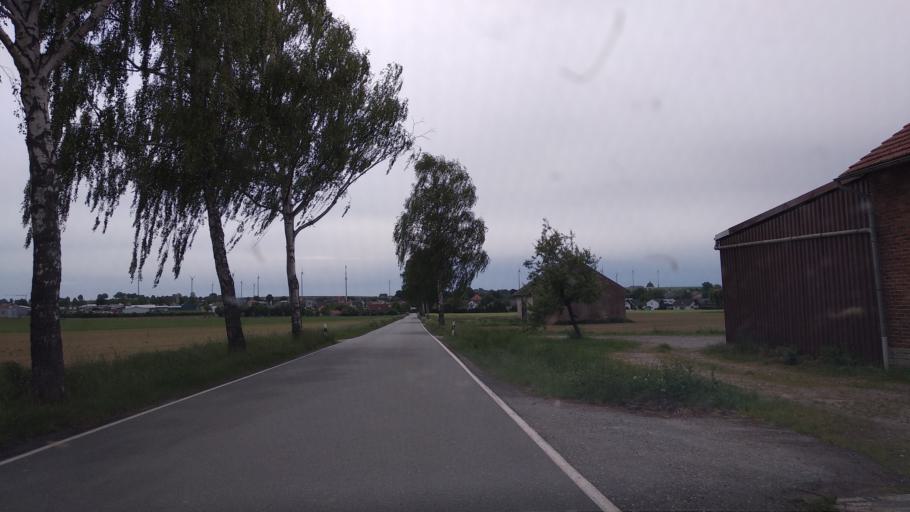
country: DE
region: North Rhine-Westphalia
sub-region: Regierungsbezirk Detmold
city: Willebadessen
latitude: 51.6064
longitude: 9.1204
